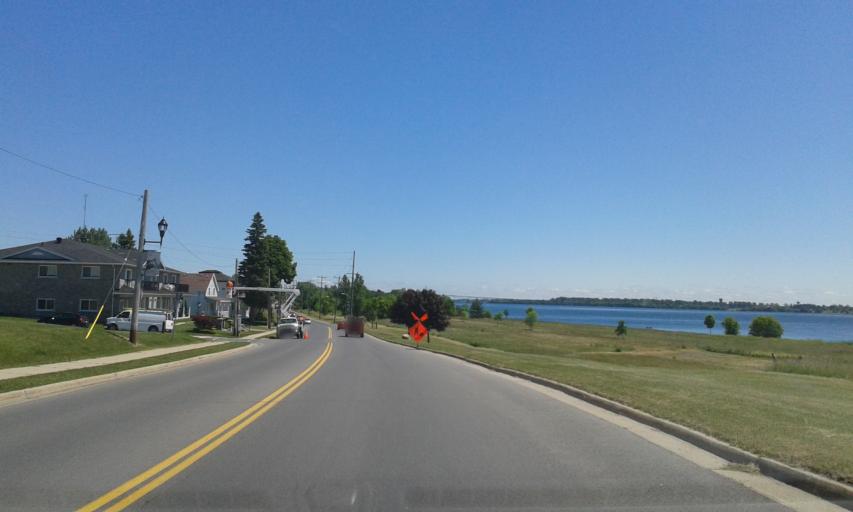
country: CA
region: Ontario
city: Prescott
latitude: 44.7123
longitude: -75.5079
